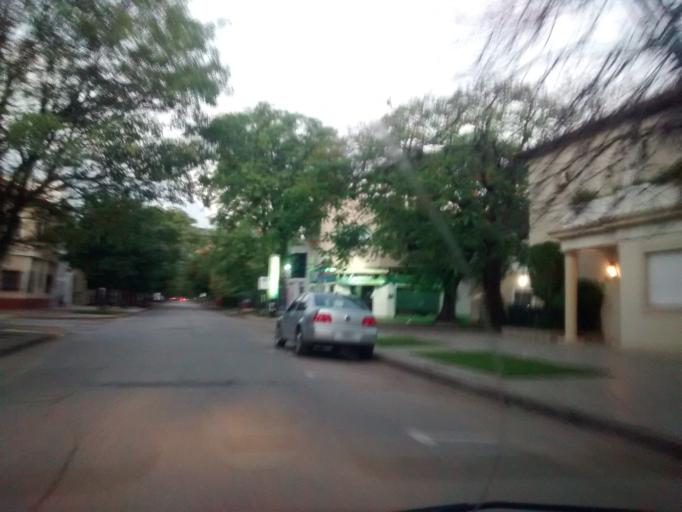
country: AR
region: Chaco
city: Resistencia
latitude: -27.4513
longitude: -58.9815
